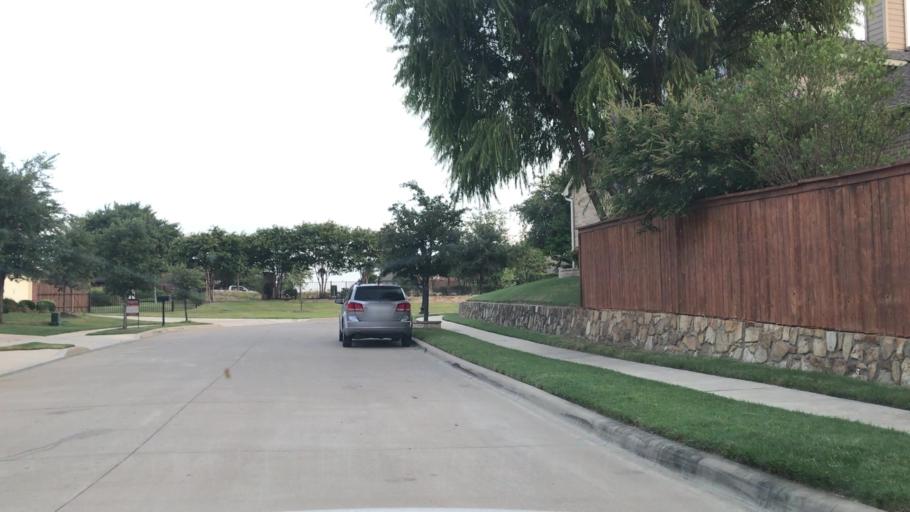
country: US
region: Texas
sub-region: Tarrant County
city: Keller
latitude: 32.9629
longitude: -97.2817
